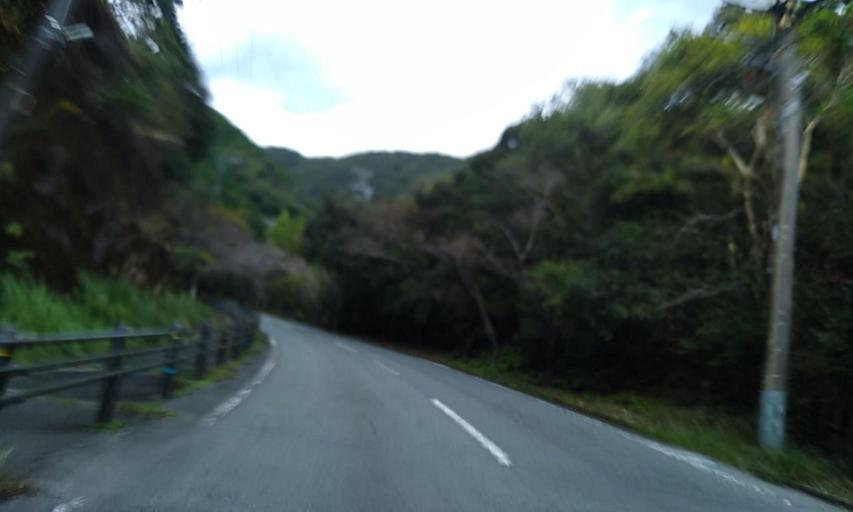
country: JP
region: Mie
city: Ise
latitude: 34.2656
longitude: 136.4889
